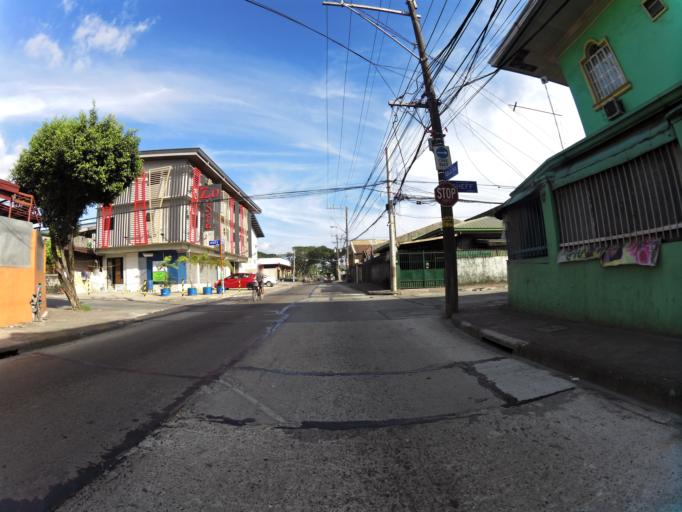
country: PH
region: Metro Manila
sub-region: Marikina
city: Calumpang
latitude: 14.6415
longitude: 121.1018
